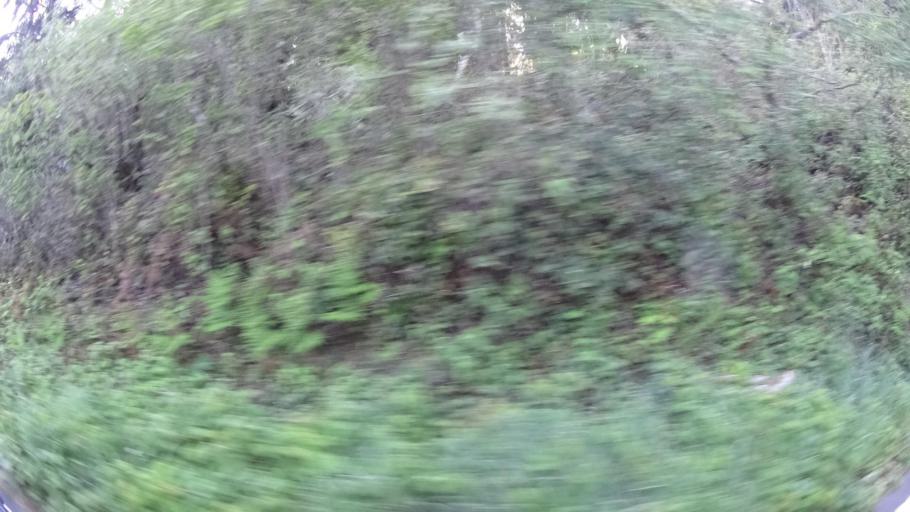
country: US
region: California
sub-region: Humboldt County
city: Westhaven-Moonstone
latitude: 41.1151
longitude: -124.1561
